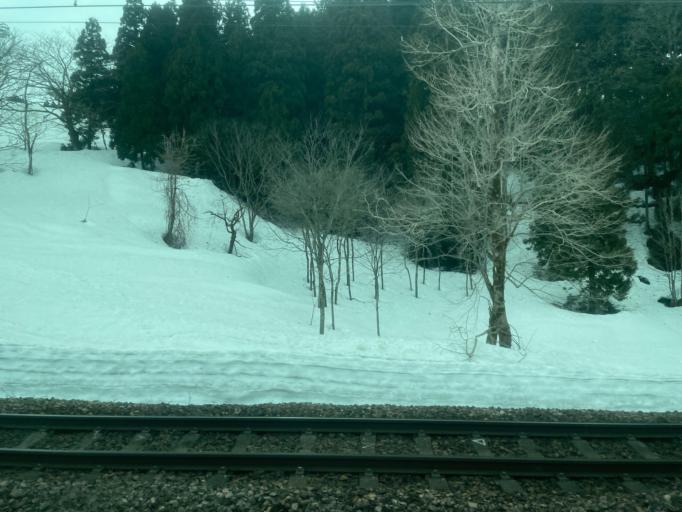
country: JP
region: Niigata
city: Shiozawa
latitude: 36.9789
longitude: 138.8008
